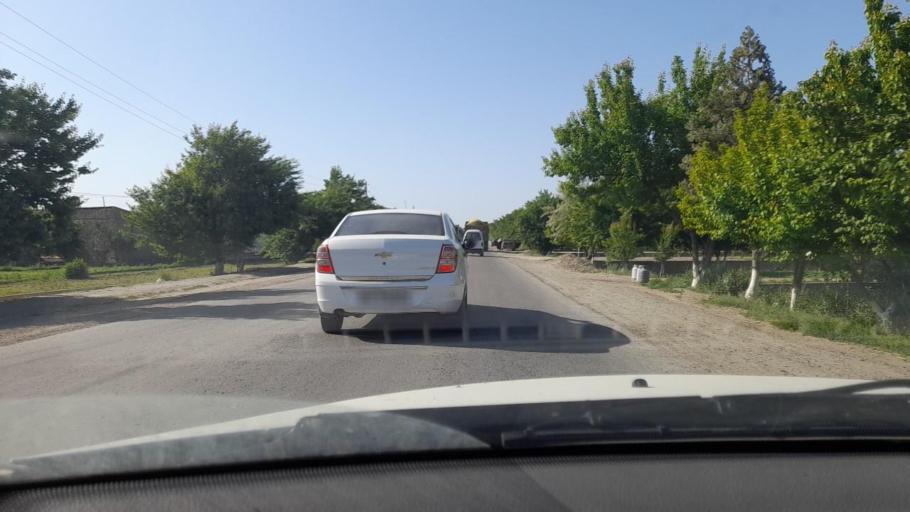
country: UZ
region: Bukhara
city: Romiton
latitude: 40.0581
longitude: 64.3278
